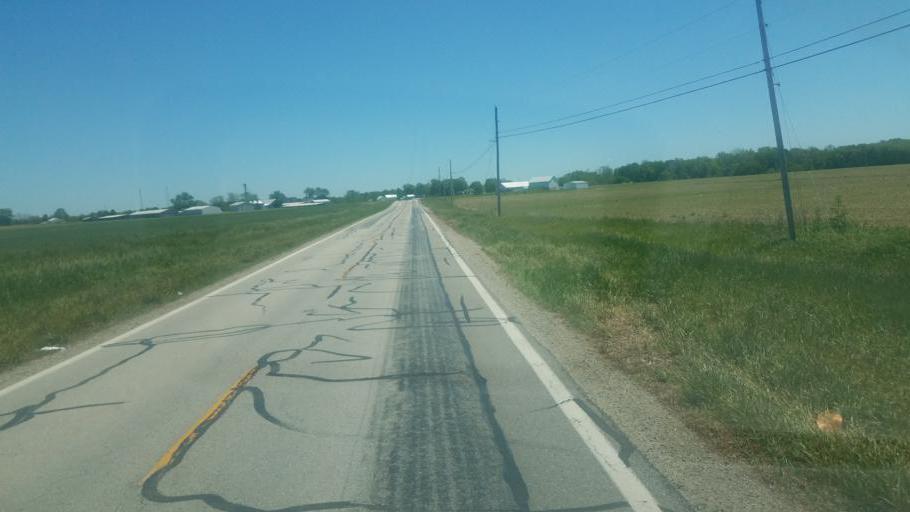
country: US
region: Ohio
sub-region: Darke County
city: Versailles
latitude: 40.2387
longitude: -84.5107
